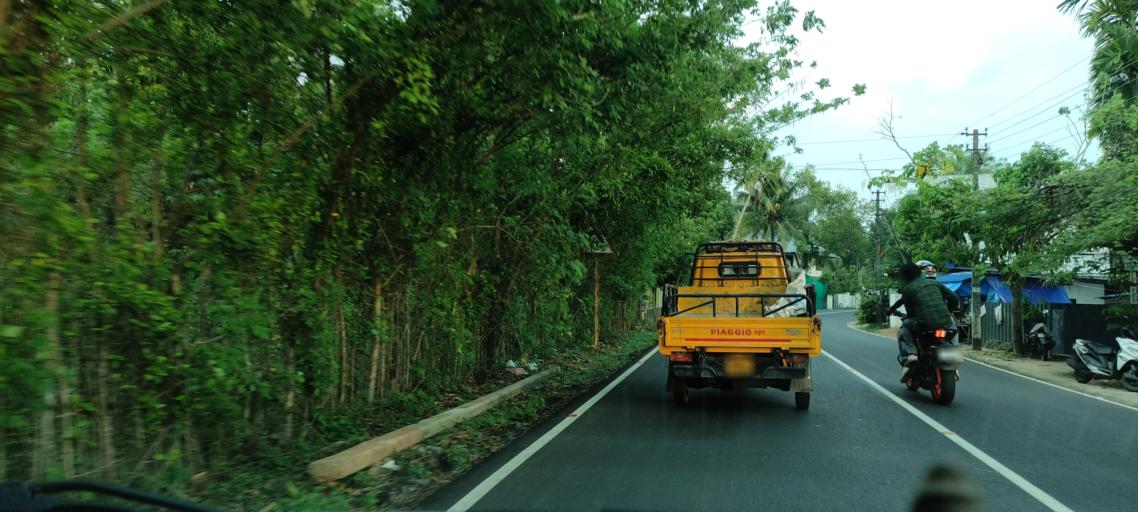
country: IN
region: Kerala
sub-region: Alappuzha
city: Kutiatodu
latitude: 9.8249
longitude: 76.3439
